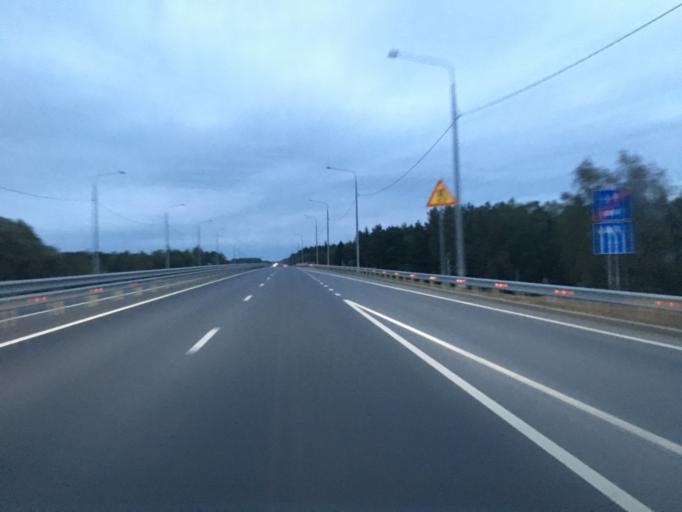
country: RU
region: Kaluga
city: Detchino
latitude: 54.9123
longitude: 36.3858
